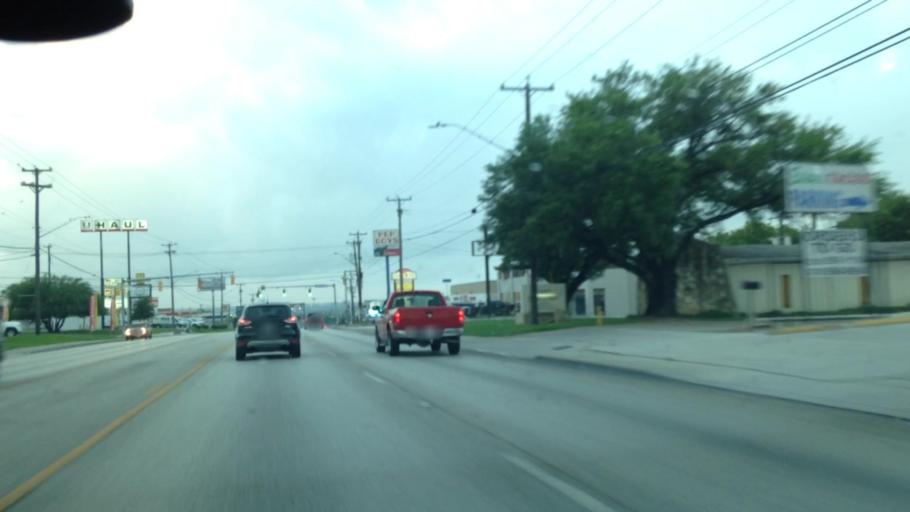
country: US
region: Texas
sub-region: Bexar County
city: Windcrest
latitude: 29.5554
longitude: -98.4011
